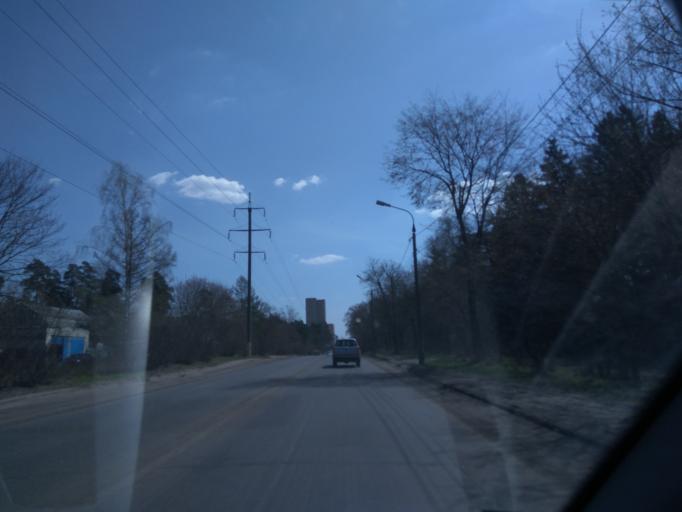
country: RU
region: Moskovskaya
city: Kratovo
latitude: 55.5707
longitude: 38.1882
